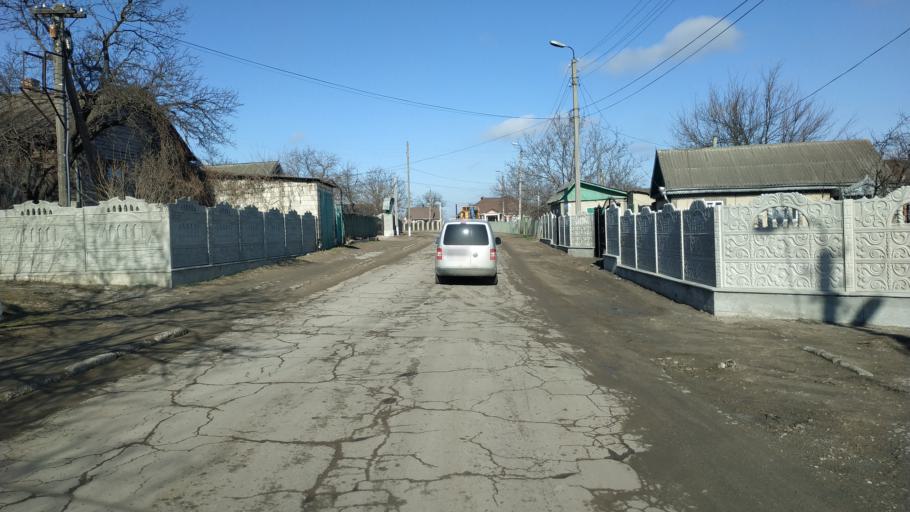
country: MD
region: Hincesti
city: Hincesti
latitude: 46.9306
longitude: 28.6494
